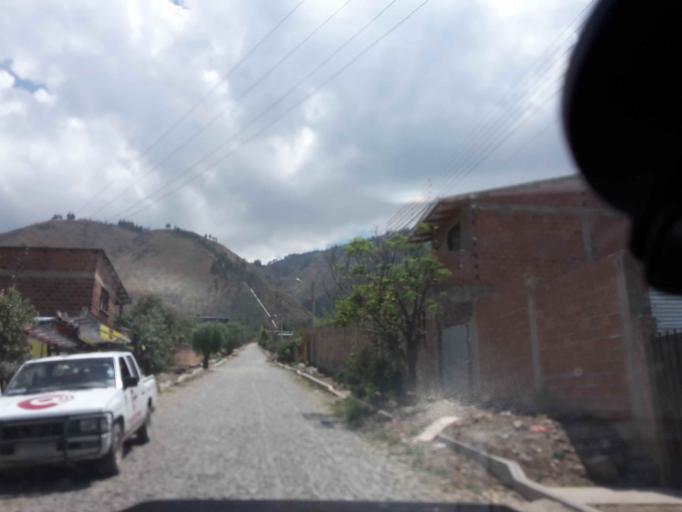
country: BO
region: Cochabamba
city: Cochabamba
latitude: -17.3236
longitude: -66.2226
